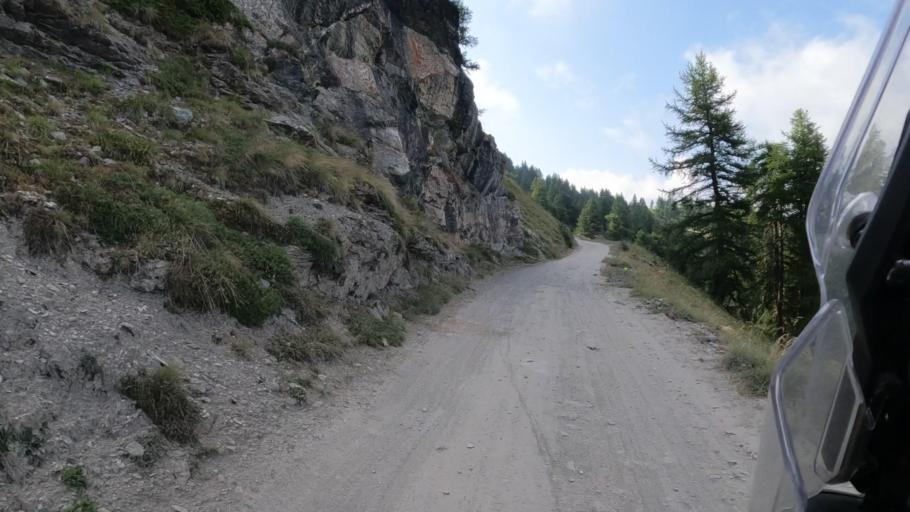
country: IT
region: Piedmont
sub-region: Provincia di Torino
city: Sauze d'Oulx
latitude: 45.0094
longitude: 6.8932
